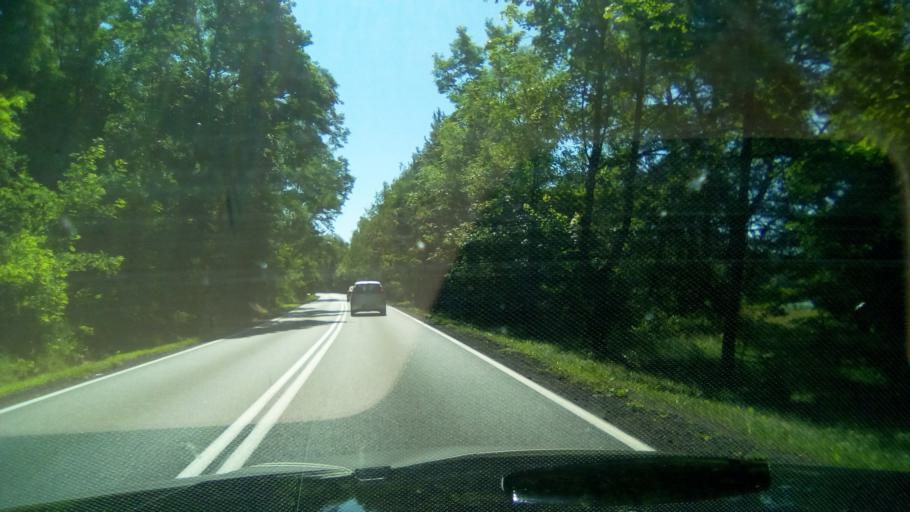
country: PL
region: Lodz Voivodeship
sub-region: Powiat tomaszowski
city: Inowlodz
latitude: 51.5234
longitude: 20.1989
